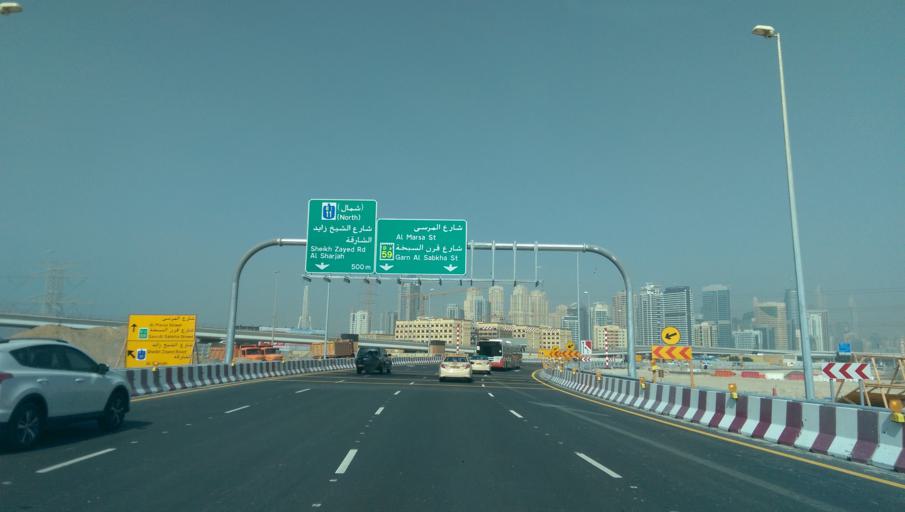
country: AE
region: Dubai
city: Dubai
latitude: 25.0580
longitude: 55.1291
